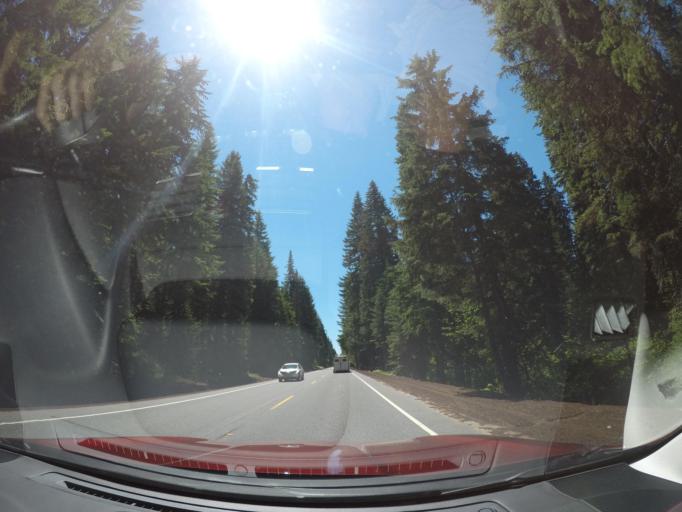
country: US
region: Oregon
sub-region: Deschutes County
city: Sisters
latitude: 44.5361
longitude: -121.9949
